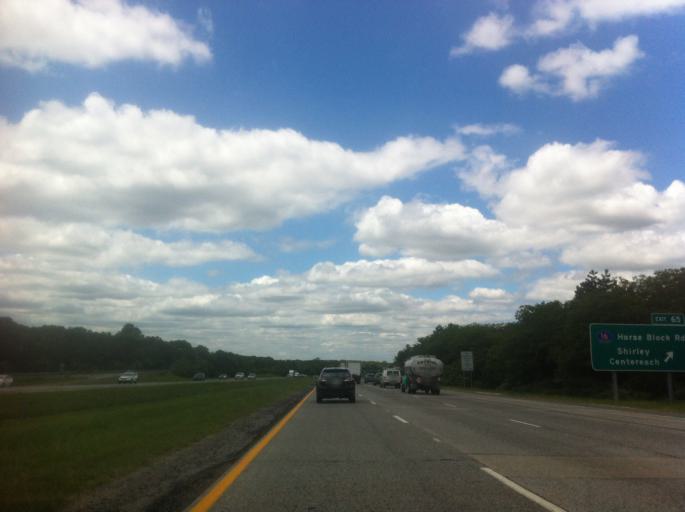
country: US
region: New York
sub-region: Suffolk County
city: Medford
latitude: 40.8235
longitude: -72.9670
